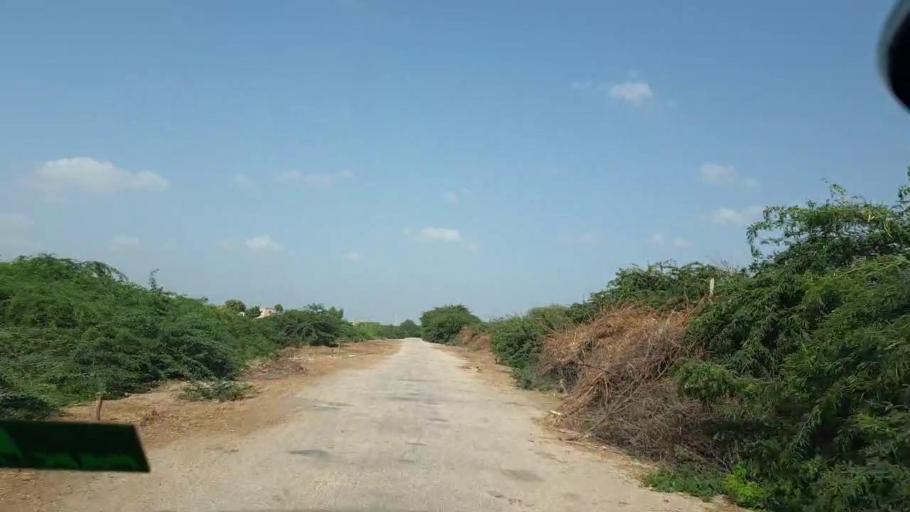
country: PK
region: Sindh
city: Tando Bago
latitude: 24.6732
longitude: 69.1936
